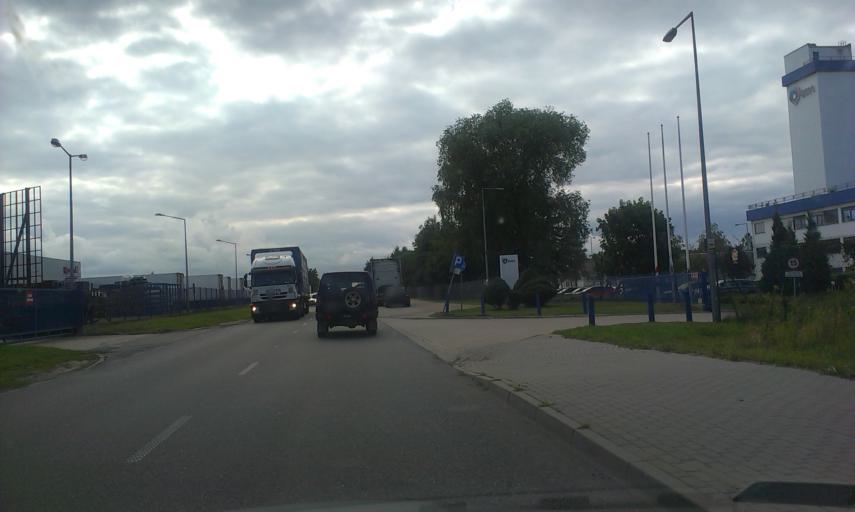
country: PL
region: Masovian Voivodeship
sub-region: Powiat zyrardowski
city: Mszczonow
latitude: 51.9730
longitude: 20.5520
